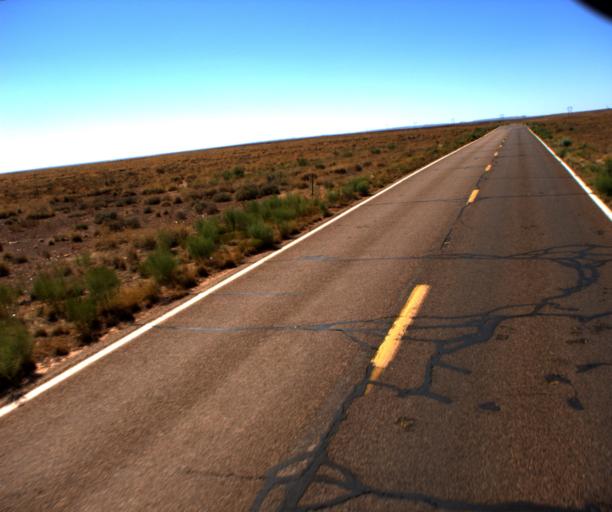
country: US
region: Arizona
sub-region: Coconino County
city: LeChee
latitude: 35.2671
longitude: -110.9726
